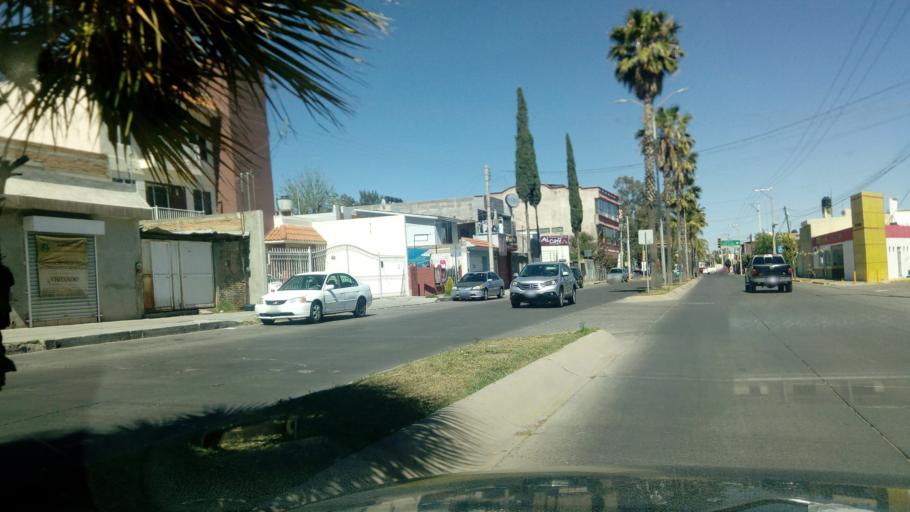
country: MX
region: Durango
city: Victoria de Durango
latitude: 24.0119
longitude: -104.6858
